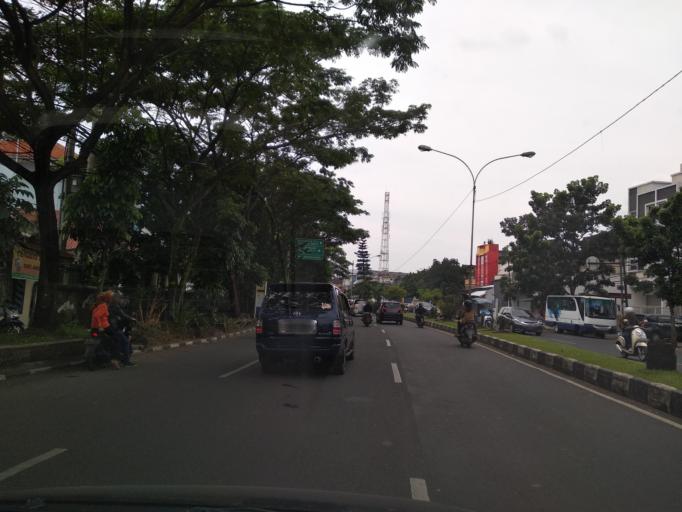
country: ID
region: West Java
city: Bandung
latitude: -6.9374
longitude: 107.5959
